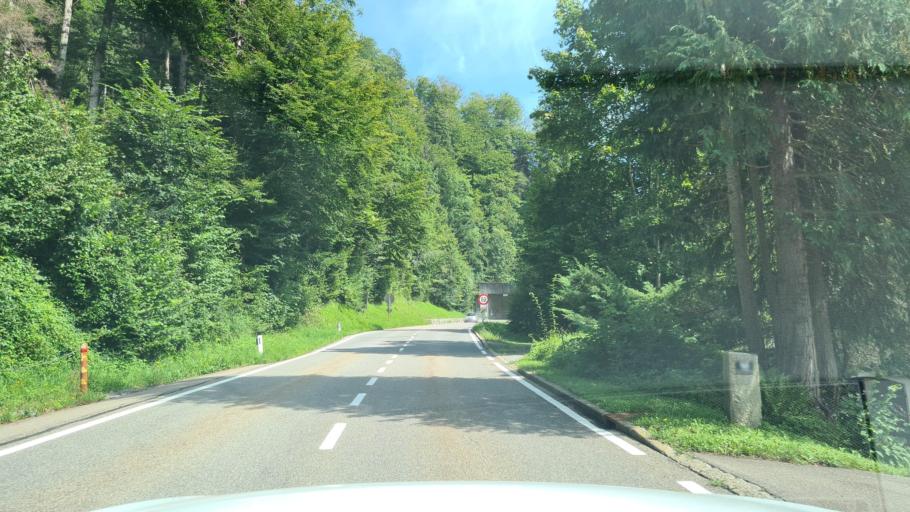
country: AT
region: Vorarlberg
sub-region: Politischer Bezirk Bregenz
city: Bildstein
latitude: 47.4458
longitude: 9.7769
